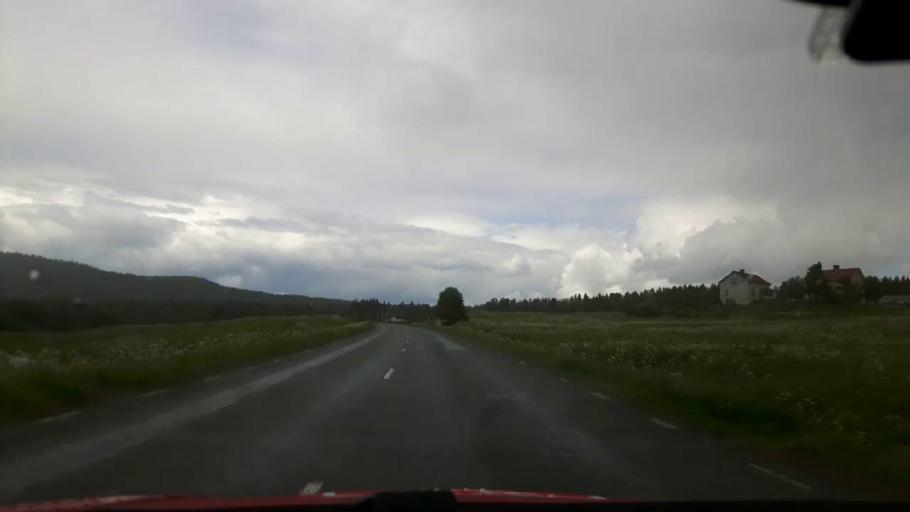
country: SE
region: Jaemtland
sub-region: Krokoms Kommun
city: Krokom
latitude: 63.4515
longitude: 14.1935
